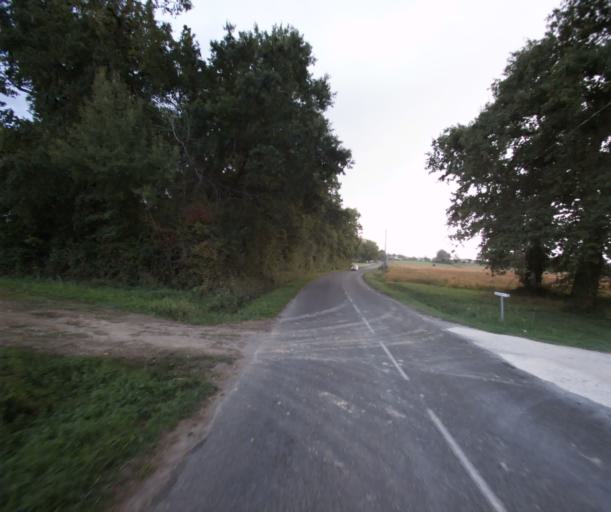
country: FR
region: Midi-Pyrenees
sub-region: Departement du Gers
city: Cazaubon
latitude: 43.9241
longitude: -0.0762
